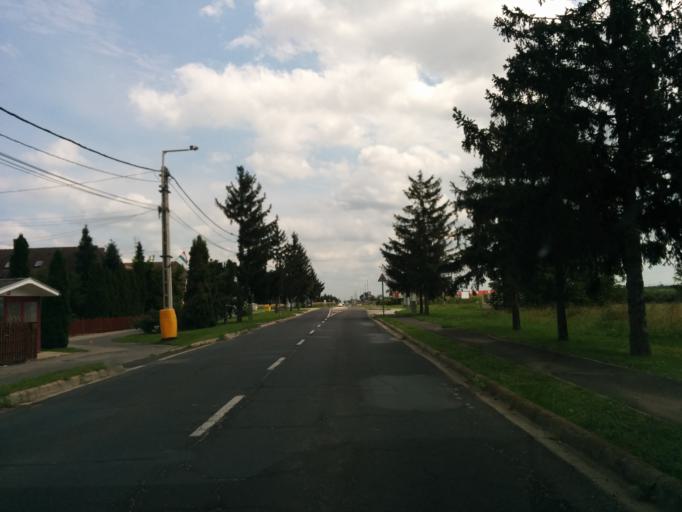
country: HU
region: Vas
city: Buk
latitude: 47.3744
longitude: 16.7673
